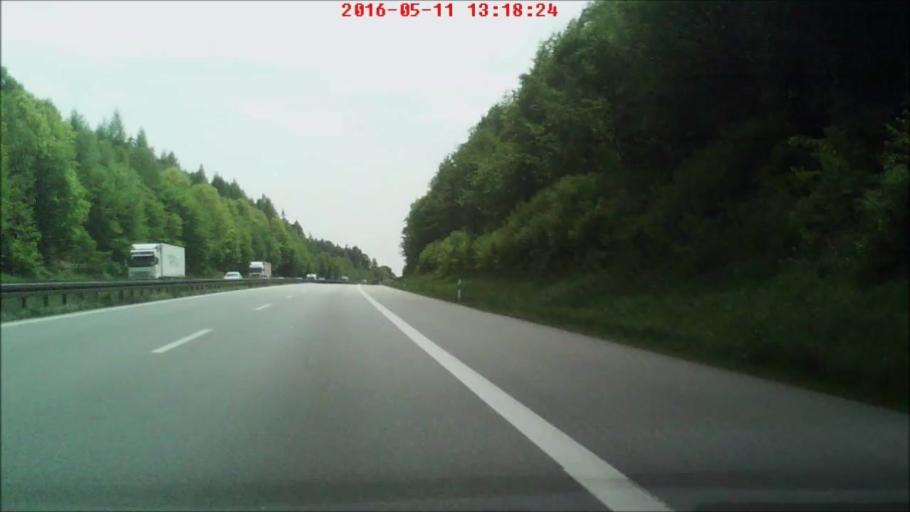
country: DE
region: Bavaria
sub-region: Lower Bavaria
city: Passau
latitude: 48.5356
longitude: 13.3998
